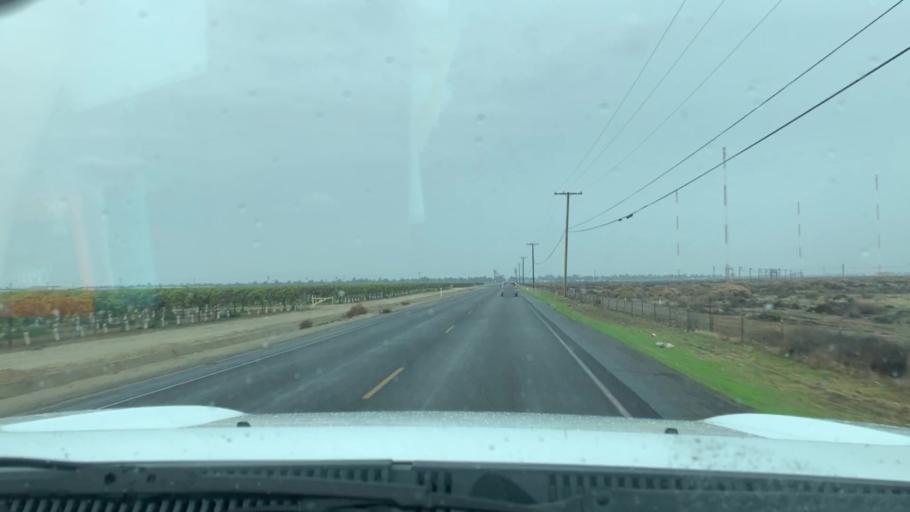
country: US
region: California
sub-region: Kern County
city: Delano
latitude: 35.7613
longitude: -119.2835
